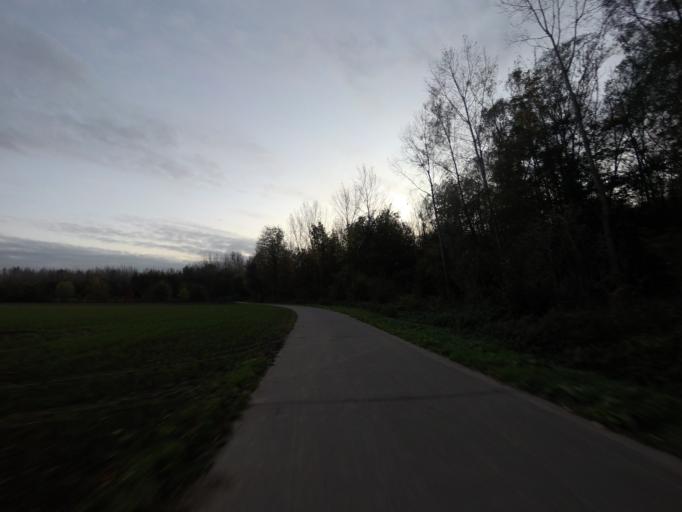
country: BE
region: Flanders
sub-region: Provincie Vlaams-Brabant
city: Steenokkerzeel
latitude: 50.9172
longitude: 4.5206
